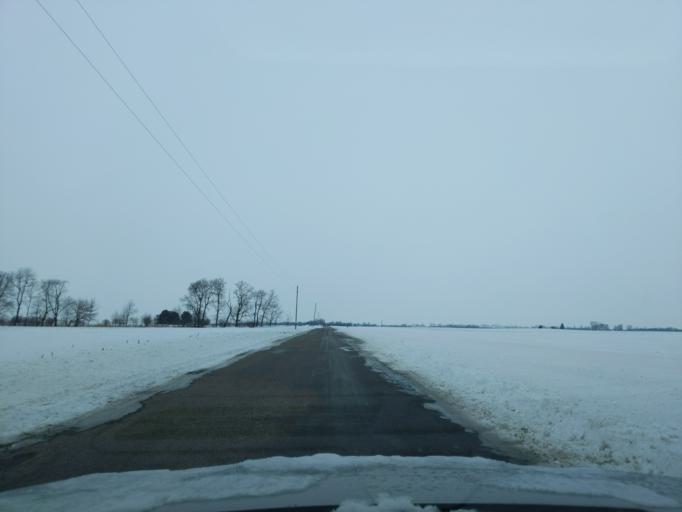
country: US
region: Indiana
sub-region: Benton County
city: Otterbein
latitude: 40.4590
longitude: -87.0927
